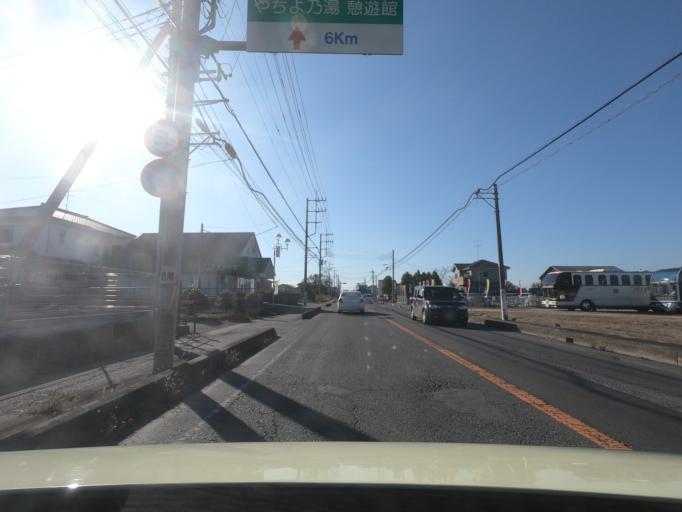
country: JP
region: Ibaraki
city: Ishige
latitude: 36.1873
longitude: 139.9290
